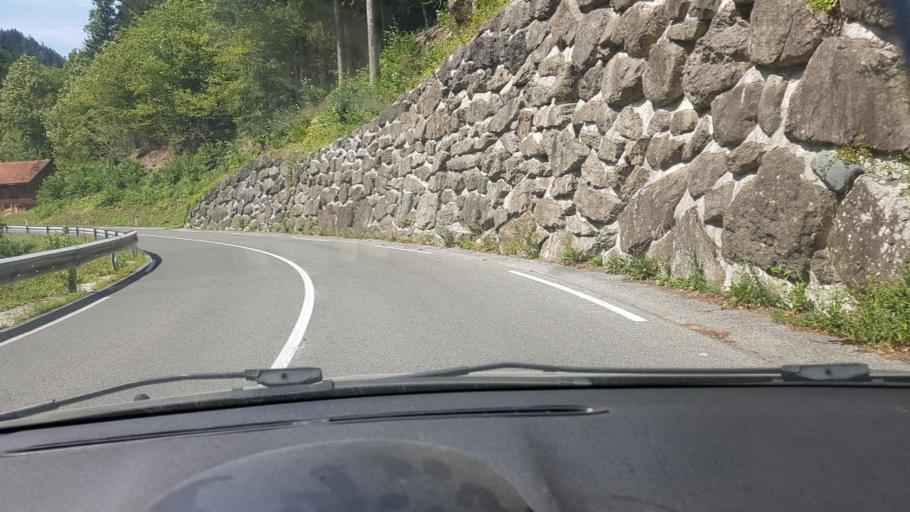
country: SI
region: Luce
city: Luce
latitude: 46.3704
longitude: 14.7915
